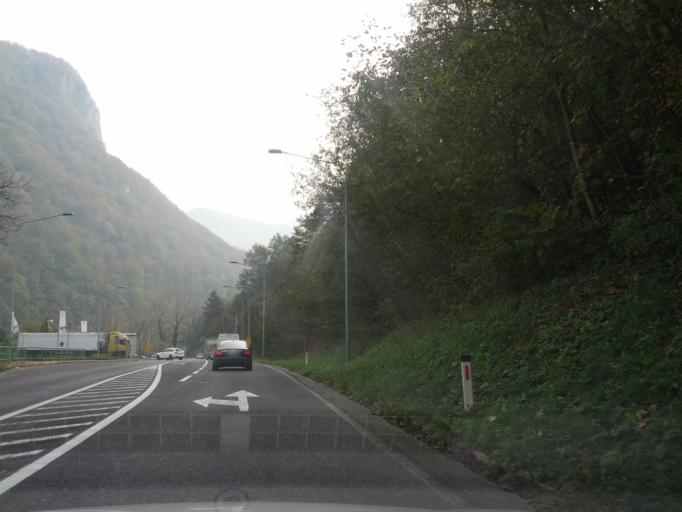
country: SI
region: Zagorje ob Savi
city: Zagorje ob Savi
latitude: 46.1189
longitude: 14.9921
